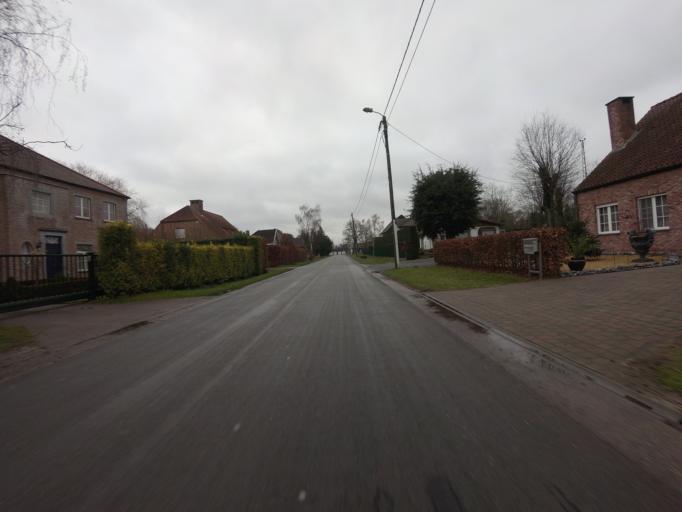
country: BE
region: Flanders
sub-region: Provincie Antwerpen
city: Sint-Katelijne-Waver
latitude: 51.0424
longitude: 4.5257
